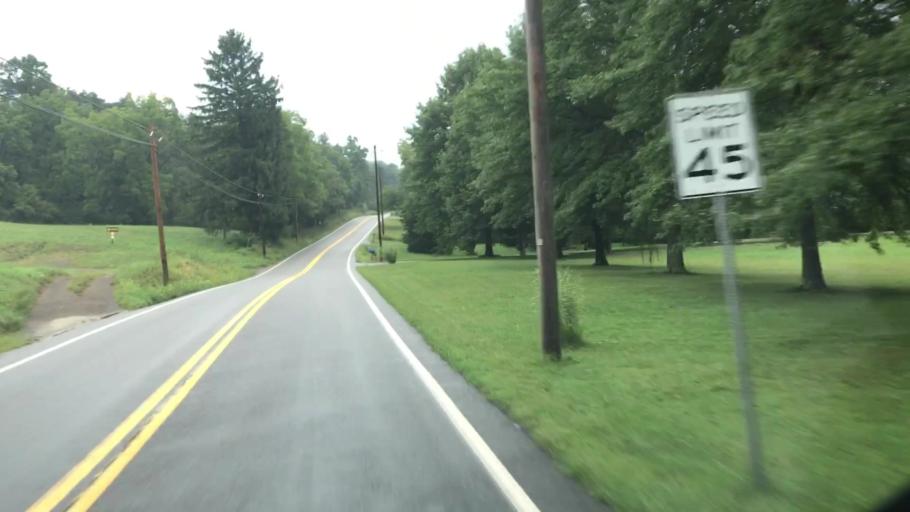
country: US
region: Pennsylvania
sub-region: Perry County
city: New Bloomfield
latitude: 40.3936
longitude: -77.1289
